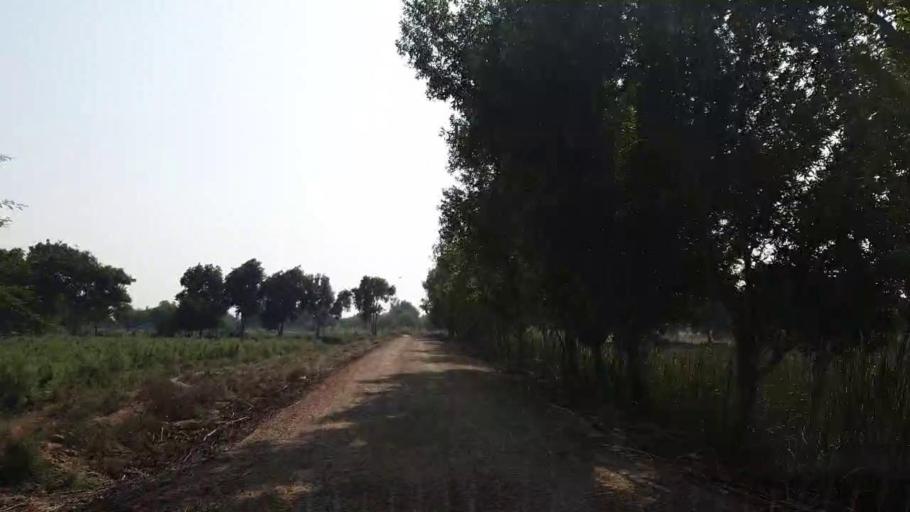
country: PK
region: Sindh
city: Tando Muhammad Khan
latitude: 25.0164
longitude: 68.4178
